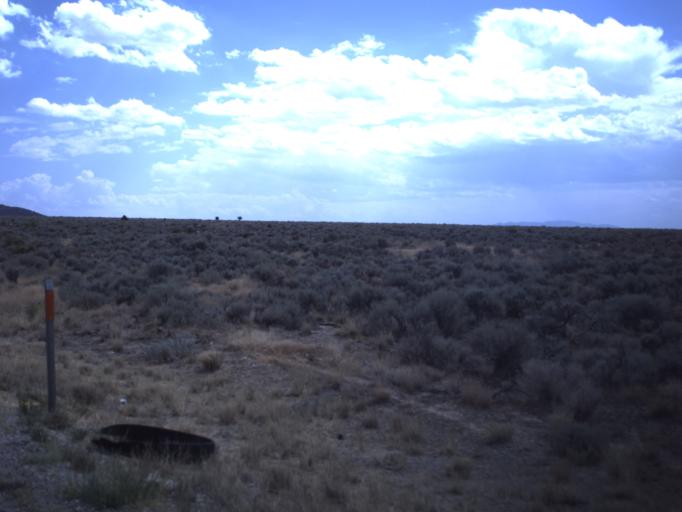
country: US
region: Utah
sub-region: Tooele County
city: Tooele
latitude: 40.3587
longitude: -112.3228
